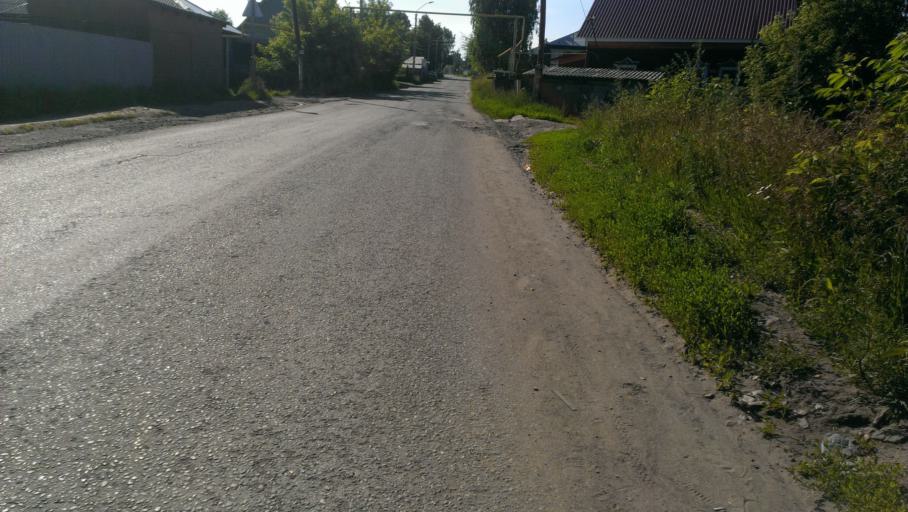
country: RU
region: Altai Krai
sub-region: Gorod Barnaulskiy
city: Barnaul
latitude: 53.3573
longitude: 83.7443
